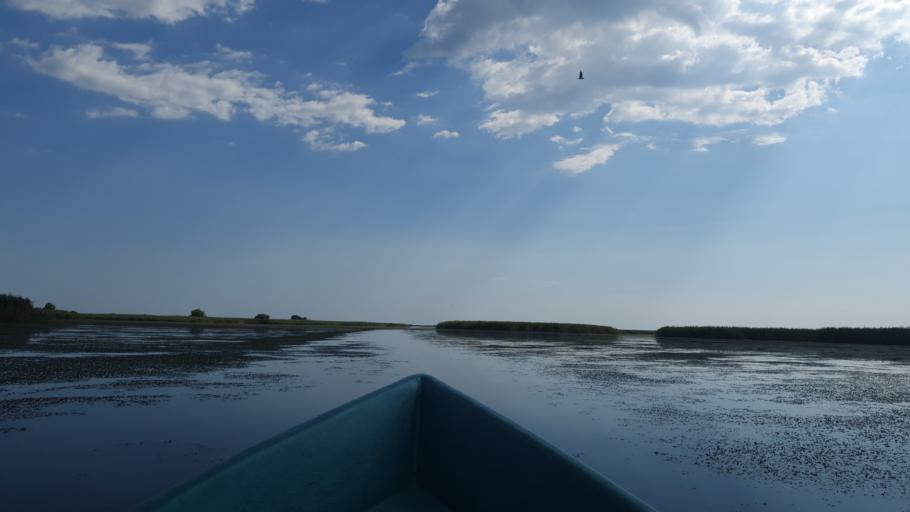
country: RU
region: Astrakhan
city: Kirovskiy
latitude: 45.8406
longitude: 48.4421
